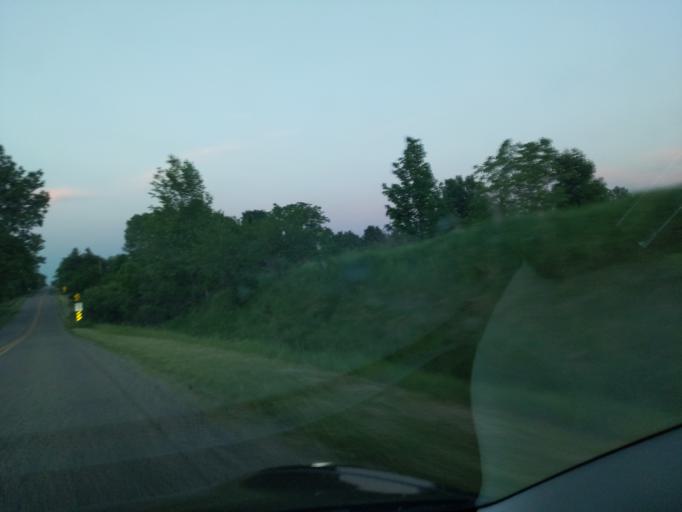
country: US
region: Michigan
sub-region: Eaton County
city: Olivet
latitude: 42.5387
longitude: -84.9690
